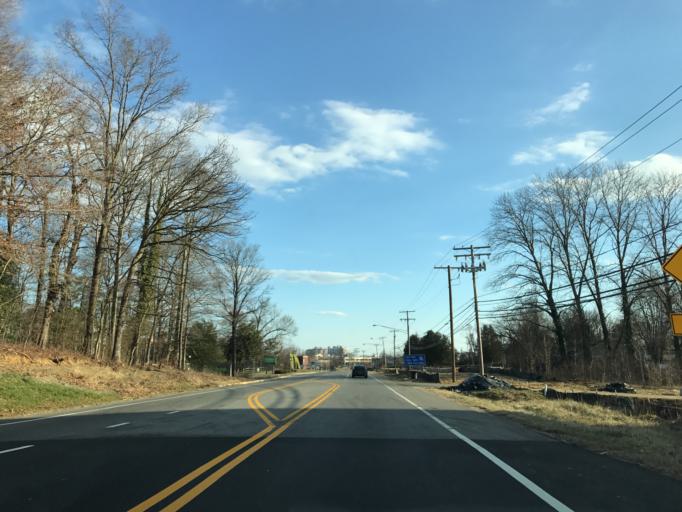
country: US
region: Maryland
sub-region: Anne Arundel County
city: Parole
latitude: 38.9945
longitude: -76.5526
